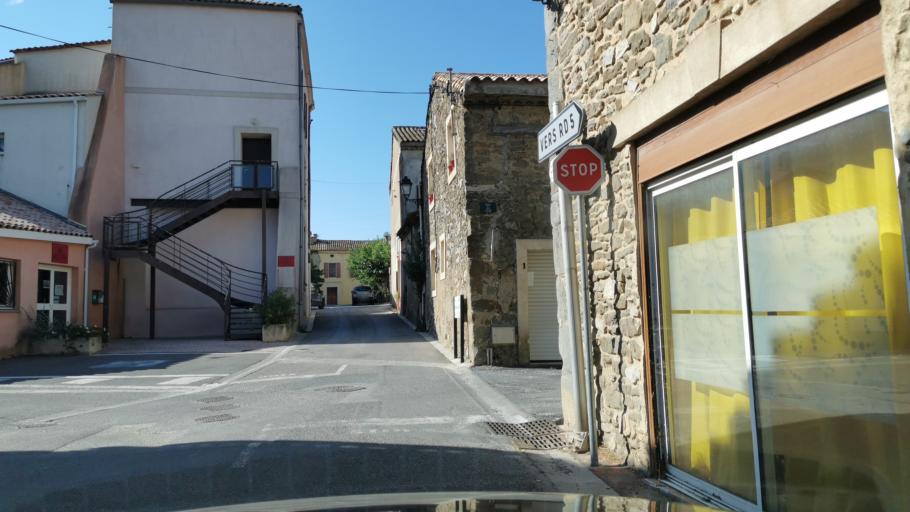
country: FR
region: Languedoc-Roussillon
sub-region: Departement de l'Aude
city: Ginestas
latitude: 43.2731
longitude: 2.8422
